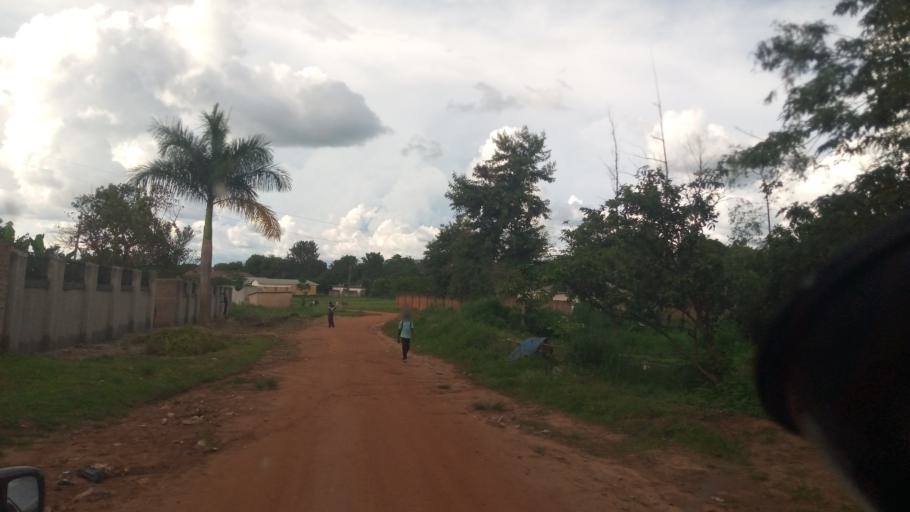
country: UG
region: Northern Region
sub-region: Lira District
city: Lira
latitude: 2.2388
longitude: 32.9004
